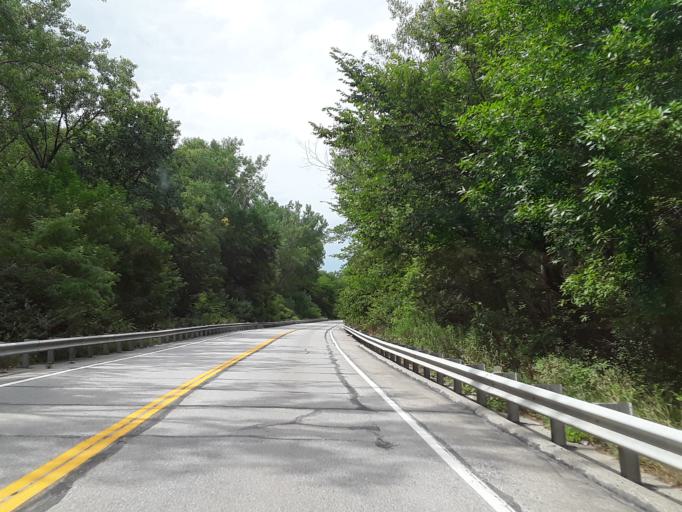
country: US
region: Iowa
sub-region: Pottawattamie County
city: Carter Lake
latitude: 41.3546
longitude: -96.0075
